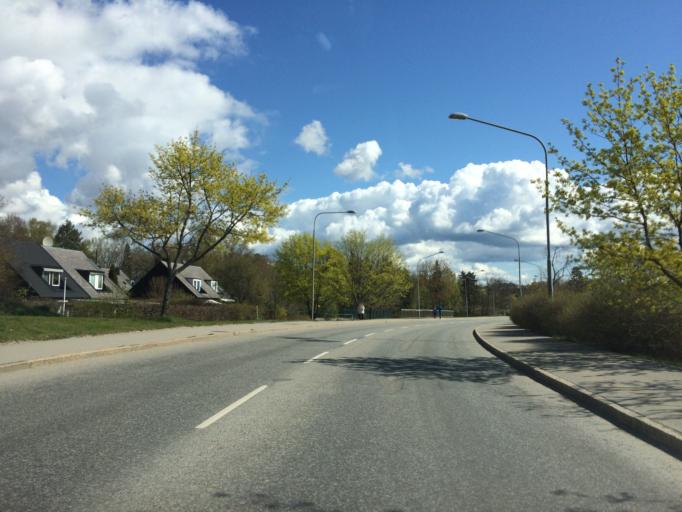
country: SE
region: Stockholm
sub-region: Huddinge Kommun
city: Segeltorp
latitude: 59.2892
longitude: 17.9159
